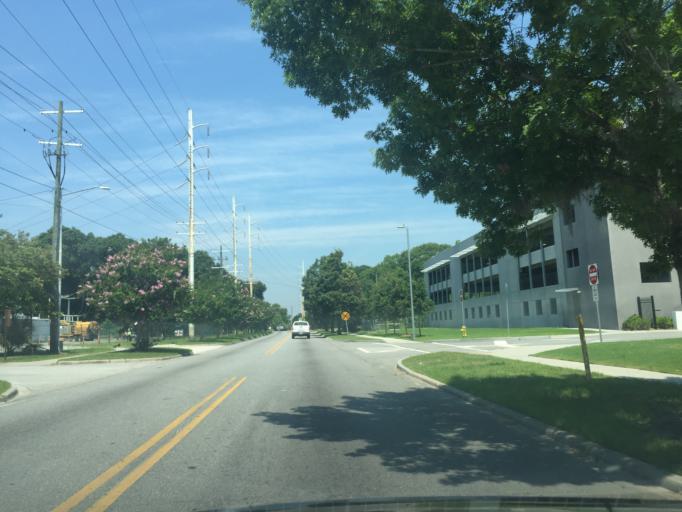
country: US
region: Georgia
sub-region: Chatham County
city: Savannah
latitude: 32.0472
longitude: -81.1094
